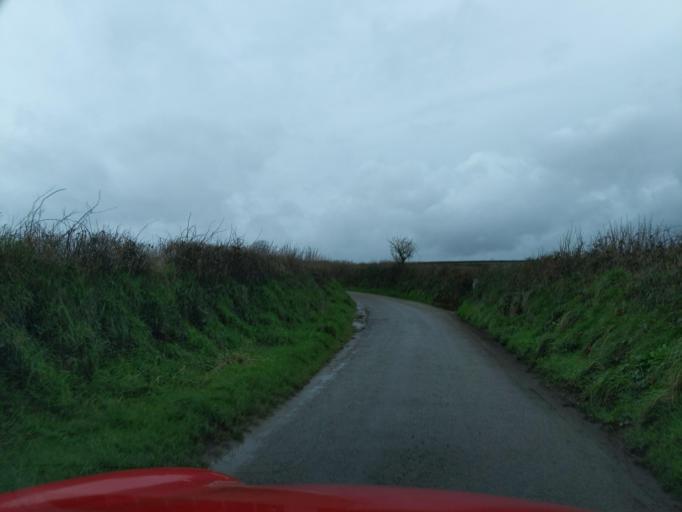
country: GB
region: England
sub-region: Cornwall
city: Duloe
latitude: 50.3479
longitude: -4.5372
